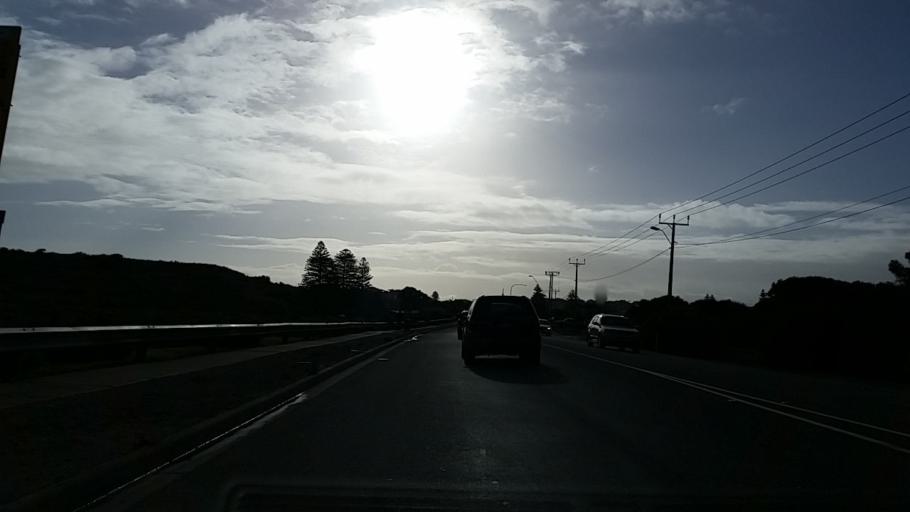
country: AU
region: South Australia
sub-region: Adelaide
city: Port Noarlunga
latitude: -35.1531
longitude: 138.4736
